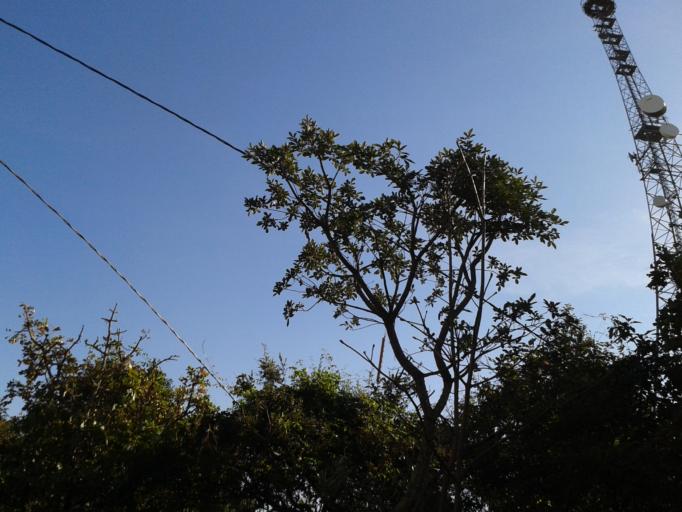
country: BR
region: Minas Gerais
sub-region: Capinopolis
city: Capinopolis
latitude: -18.7622
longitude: -49.5401
